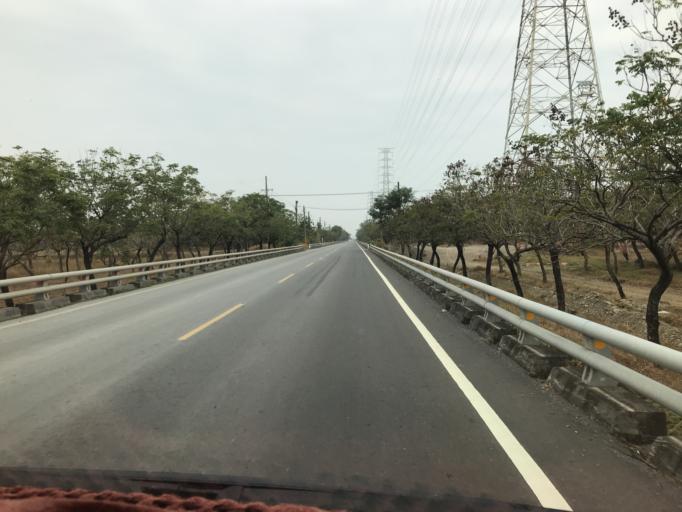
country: TW
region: Taiwan
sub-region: Pingtung
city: Pingtung
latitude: 22.4393
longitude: 120.6045
